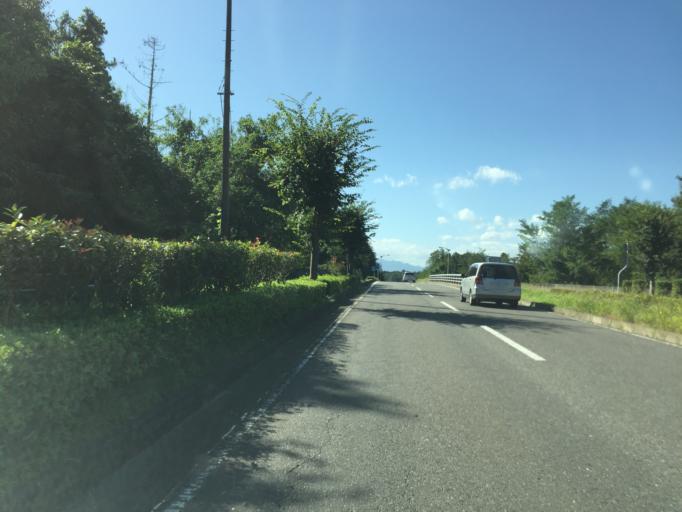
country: JP
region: Fukushima
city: Sukagawa
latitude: 37.2653
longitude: 140.4091
